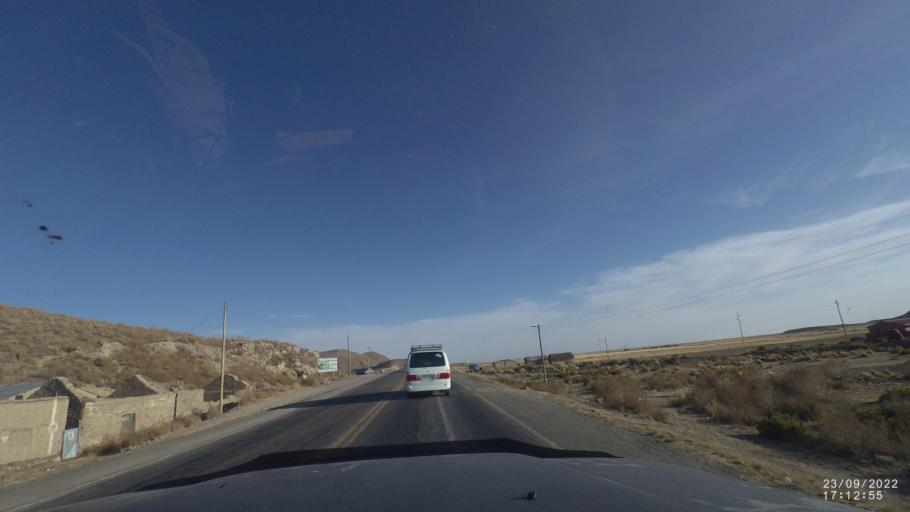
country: BO
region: Oruro
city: Totoral
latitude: -18.7079
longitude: -66.8754
